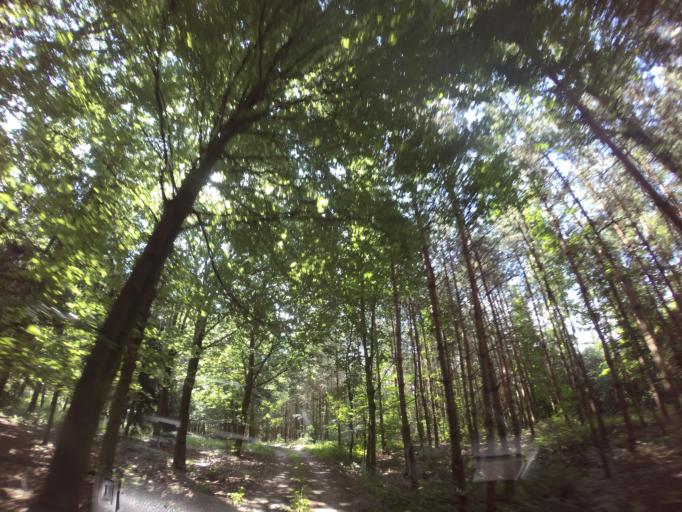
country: PL
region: West Pomeranian Voivodeship
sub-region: Powiat choszczenski
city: Bierzwnik
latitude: 52.9747
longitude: 15.5984
